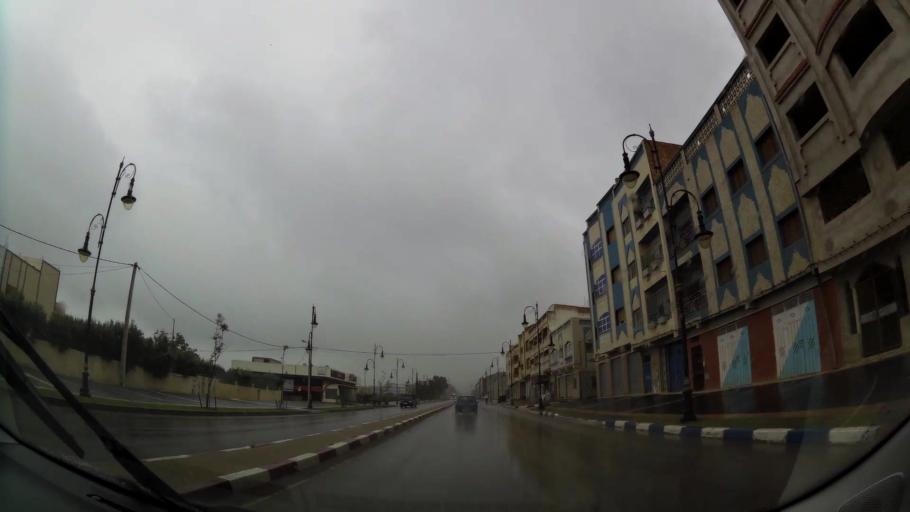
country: MA
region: Taza-Al Hoceima-Taounate
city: Imzourene
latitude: 35.1130
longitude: -3.8417
